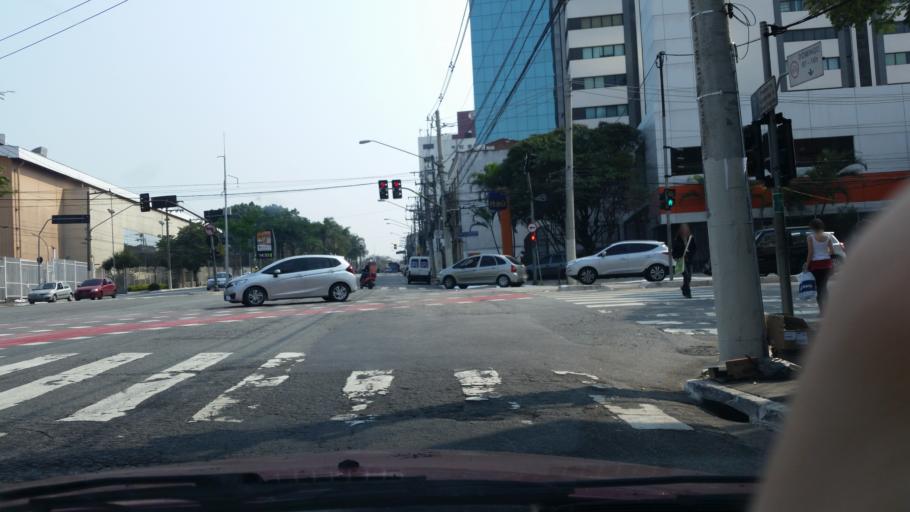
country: BR
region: Sao Paulo
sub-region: Diadema
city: Diadema
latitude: -23.6281
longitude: -46.6441
